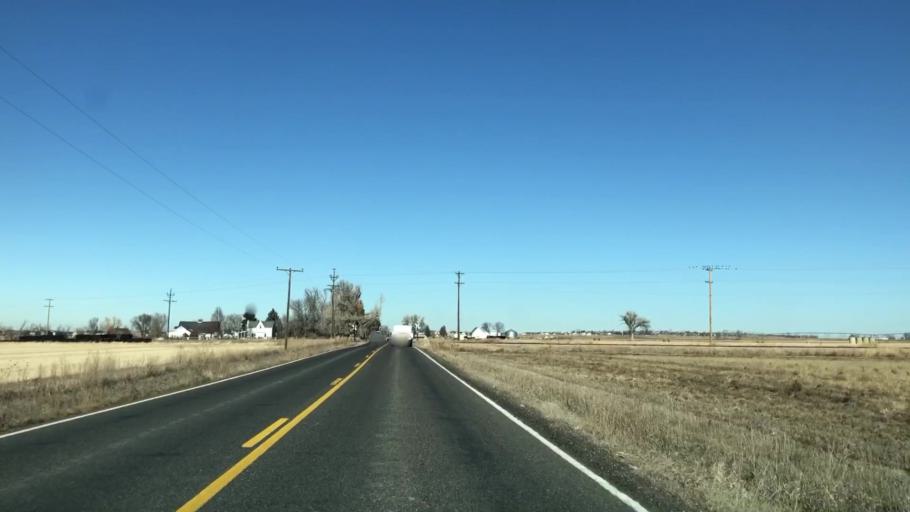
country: US
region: Colorado
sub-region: Weld County
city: Windsor
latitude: 40.5036
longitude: -104.9441
